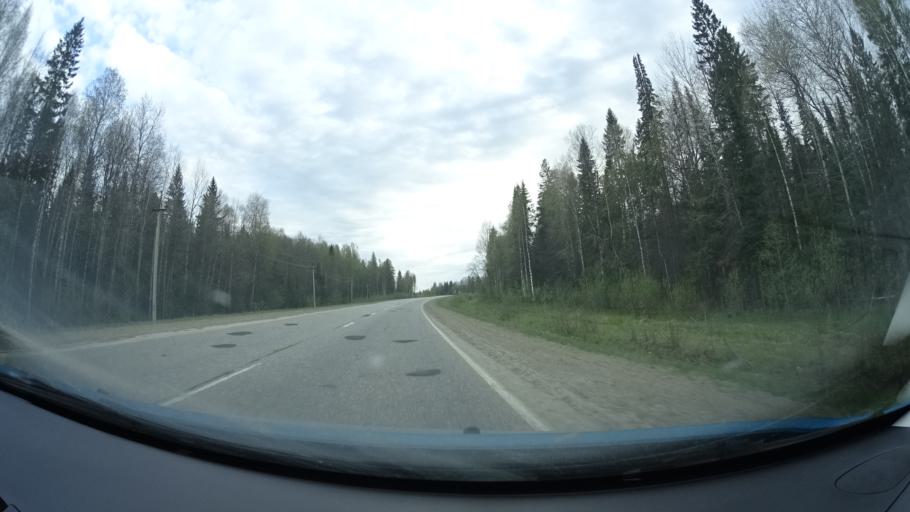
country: RU
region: Perm
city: Osa
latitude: 57.4351
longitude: 55.6261
